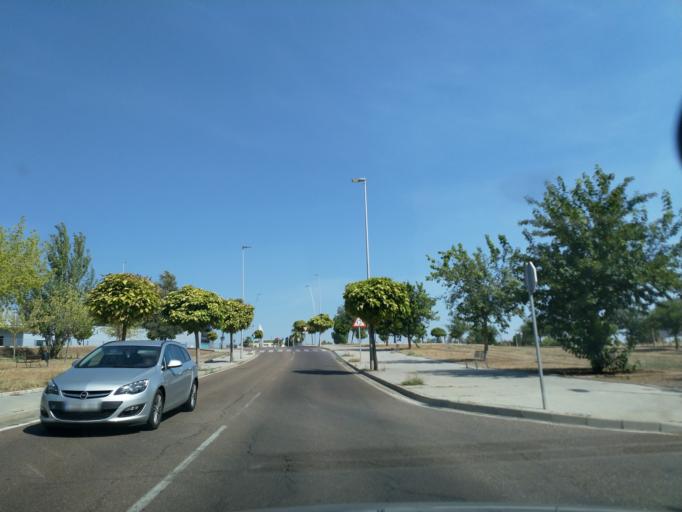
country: ES
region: Extremadura
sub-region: Provincia de Badajoz
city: Merida
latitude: 38.9342
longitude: -6.3460
